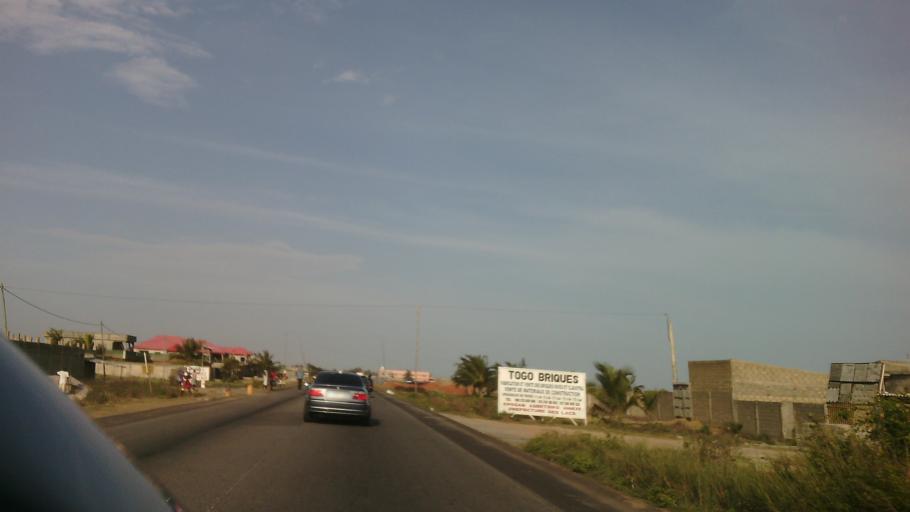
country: TG
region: Maritime
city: Lome
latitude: 6.1794
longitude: 1.3832
